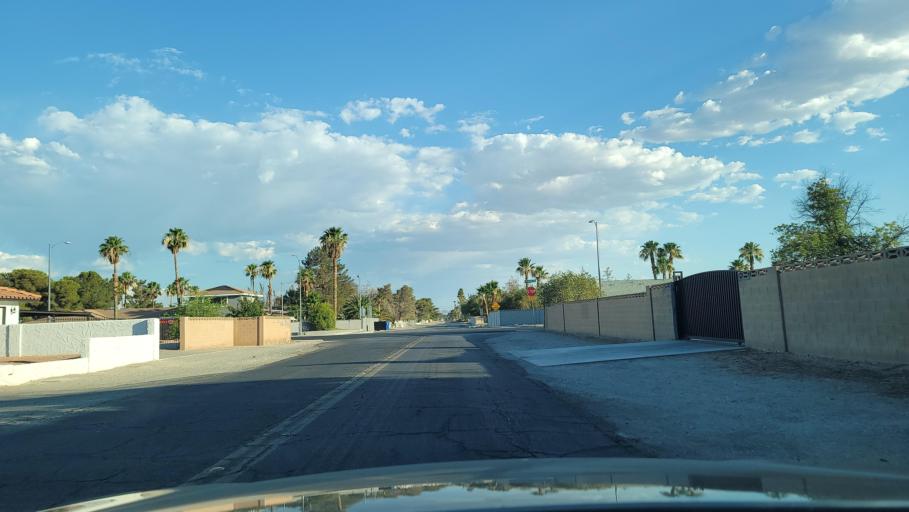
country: US
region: Nevada
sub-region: Clark County
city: Spring Valley
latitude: 36.1525
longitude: -115.2190
